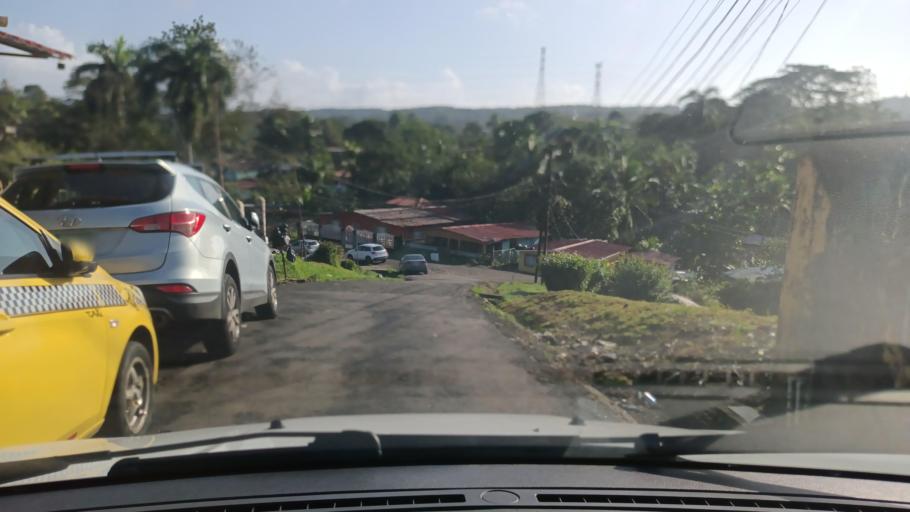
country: PA
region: Colon
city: Sabanitas
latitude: 9.3430
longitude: -79.8031
